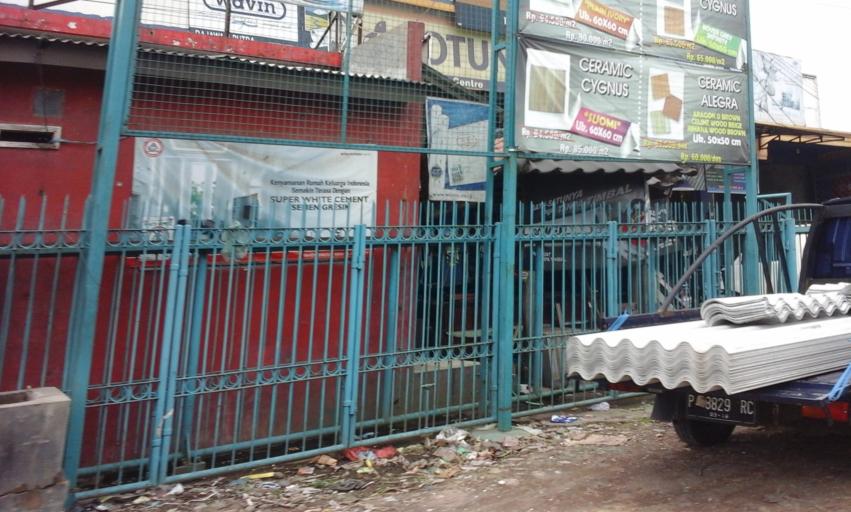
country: ID
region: East Java
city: Dukuhsia
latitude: -8.2017
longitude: 113.6200
